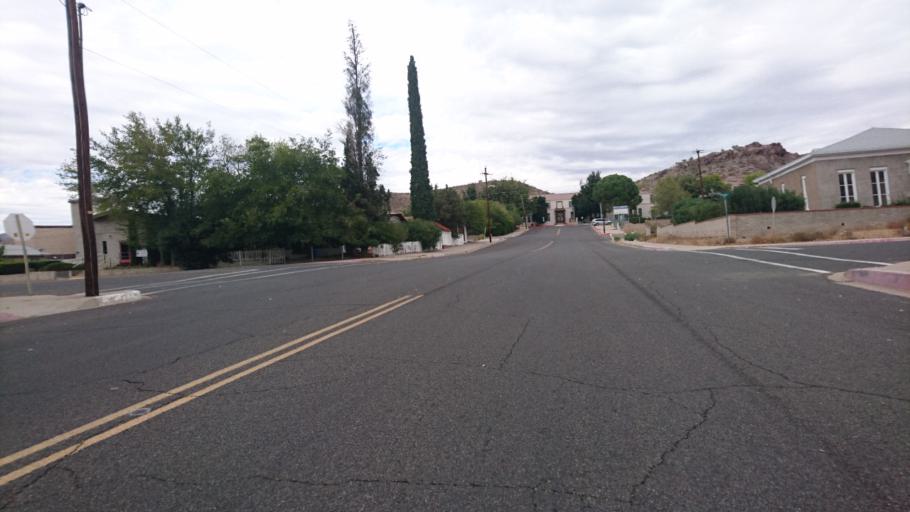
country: US
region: Arizona
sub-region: Mohave County
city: Kingman
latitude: 35.1913
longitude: -114.0511
